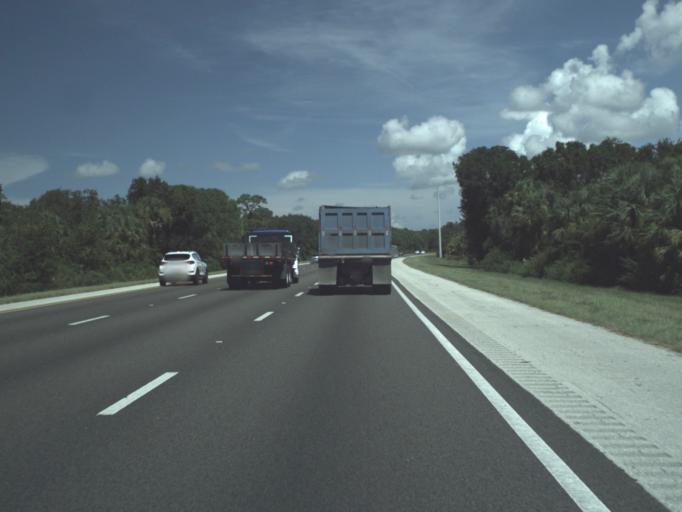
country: US
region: Florida
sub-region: Sarasota County
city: Vamo
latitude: 27.2243
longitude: -82.4498
